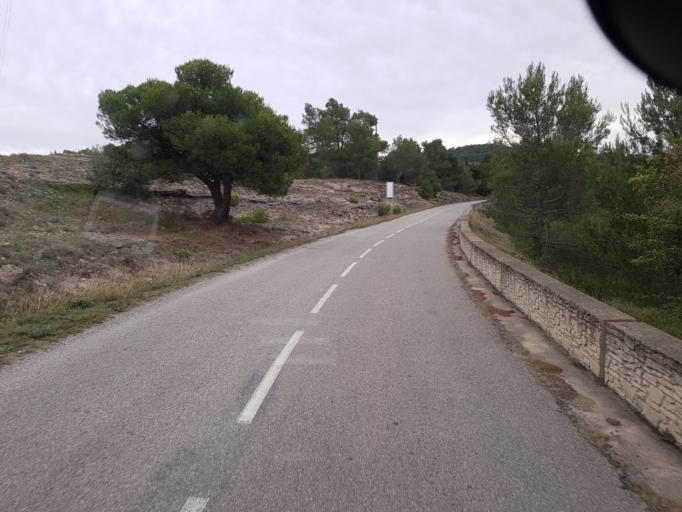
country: FR
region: Languedoc-Roussillon
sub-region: Departement de l'Aude
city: Conques-sur-Orbiel
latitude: 43.3050
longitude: 2.4654
